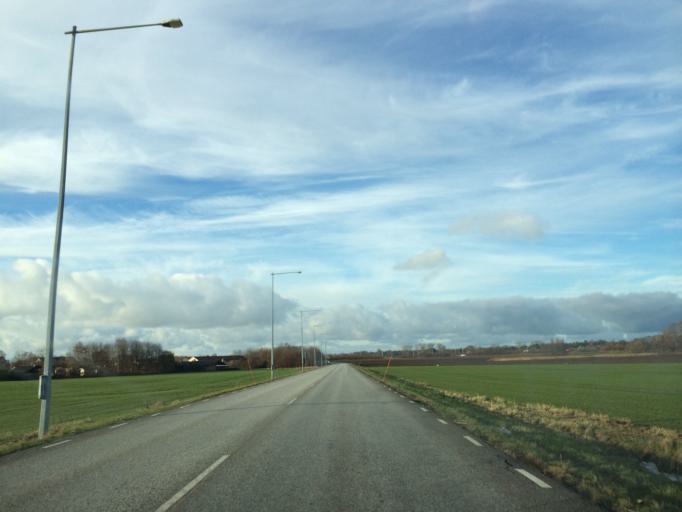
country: SE
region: Skane
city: Bjarred
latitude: 55.7237
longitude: 13.0397
